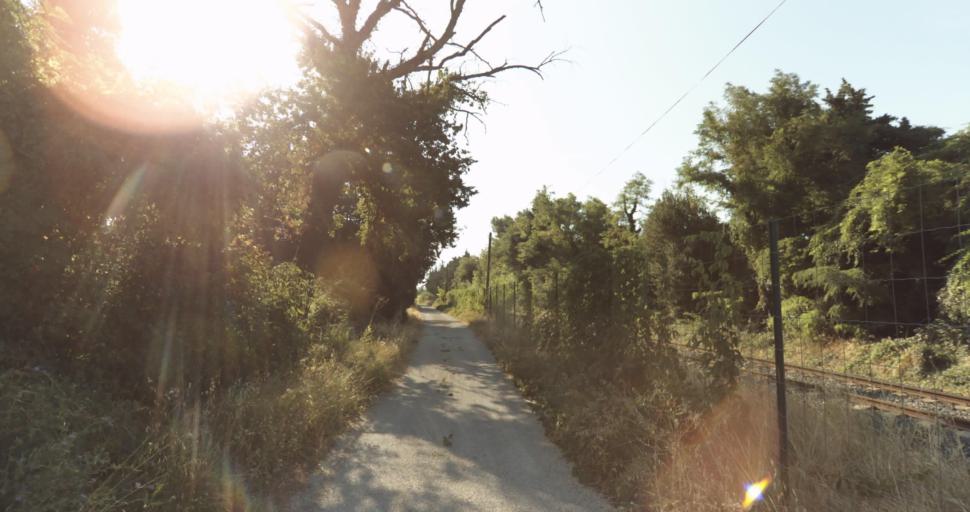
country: FR
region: Provence-Alpes-Cote d'Azur
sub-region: Departement du Vaucluse
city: Monteux
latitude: 44.0332
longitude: 5.0093
